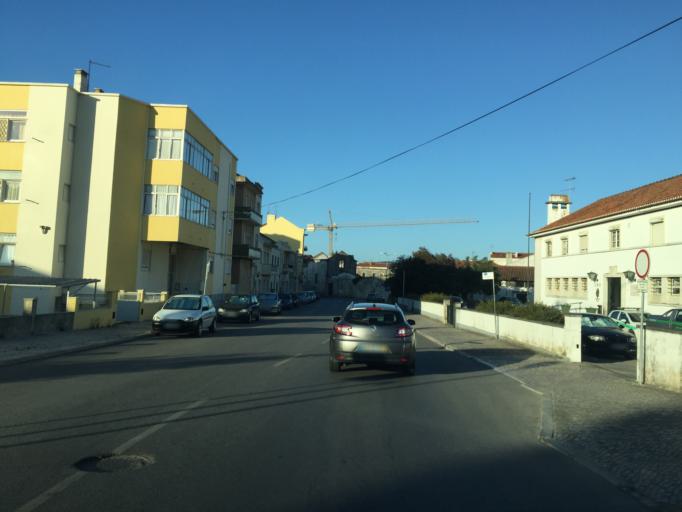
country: PT
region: Lisbon
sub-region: Torres Vedras
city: Torres Vedras
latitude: 39.0915
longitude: -9.2641
